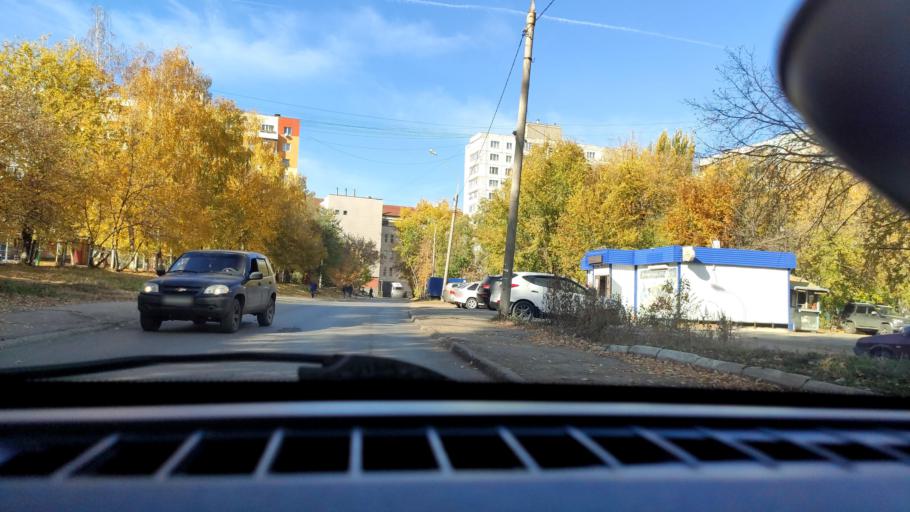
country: RU
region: Samara
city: Samara
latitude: 53.2444
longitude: 50.2180
